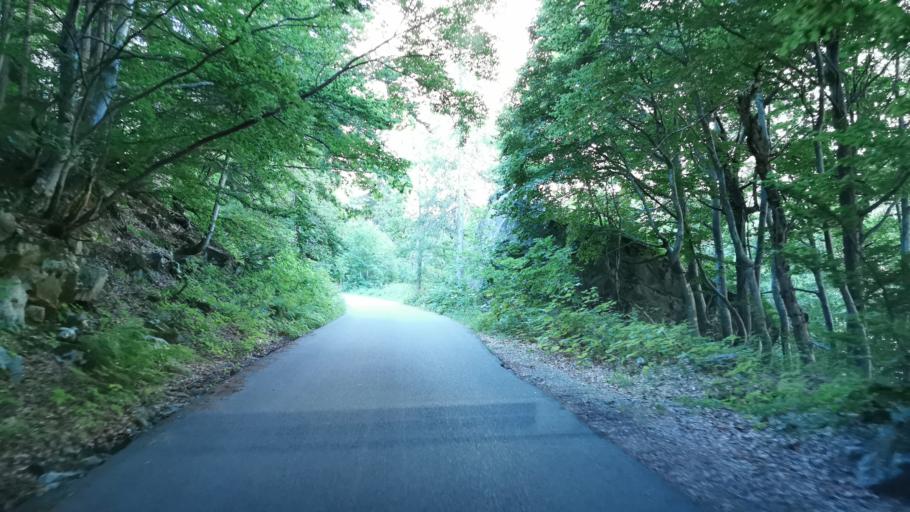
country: IT
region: Piedmont
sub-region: Provincia di Cuneo
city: Demonte
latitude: 44.2047
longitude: 7.2712
